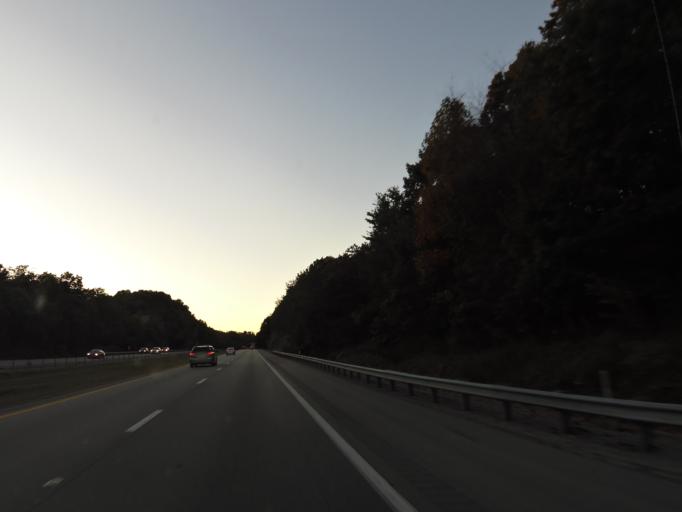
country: US
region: Kentucky
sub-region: Rockcastle County
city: Mount Vernon
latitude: 37.3033
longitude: -84.2825
